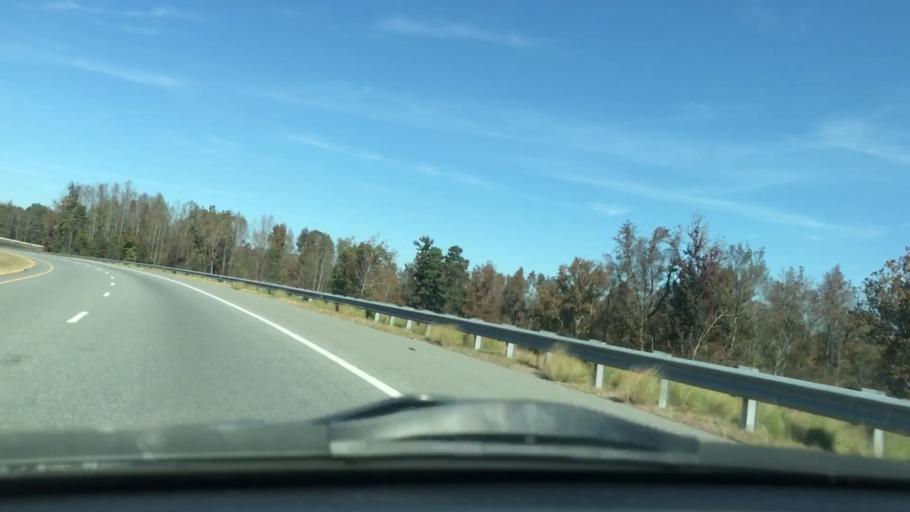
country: US
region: North Carolina
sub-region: Randolph County
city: Archdale
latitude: 35.8993
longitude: -79.9115
